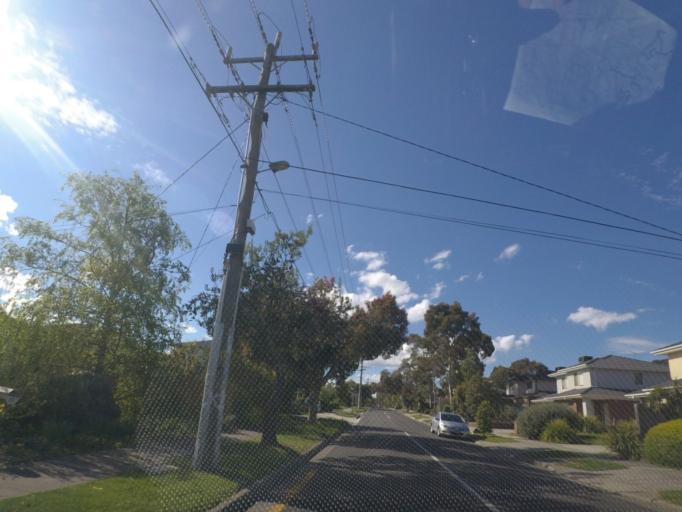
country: AU
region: Victoria
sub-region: Knox
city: Knoxfield
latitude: -37.8911
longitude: 145.2491
